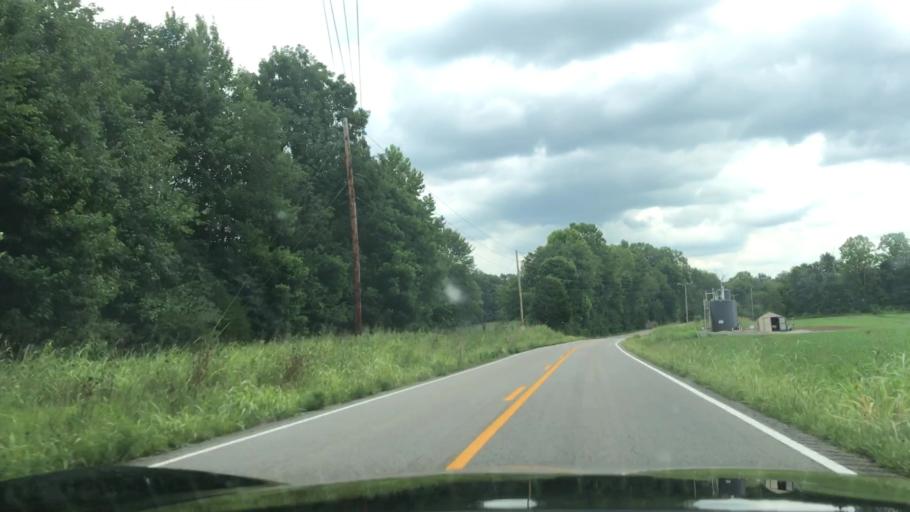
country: US
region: Kentucky
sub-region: Muhlenberg County
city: Central City
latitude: 37.2033
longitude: -87.0237
